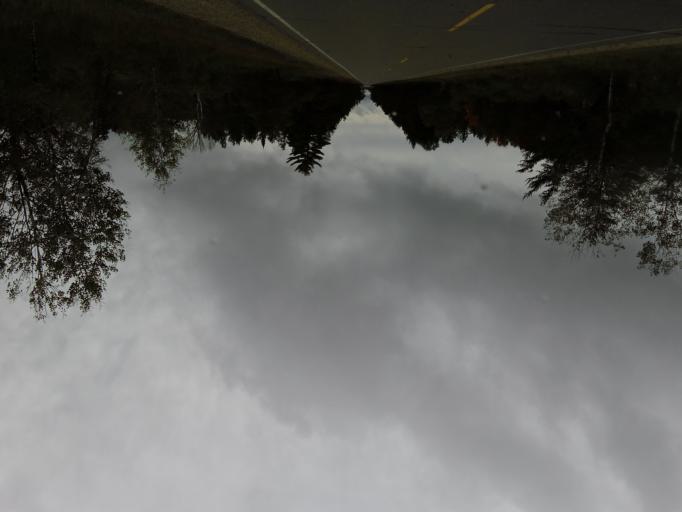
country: US
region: Michigan
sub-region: Roscommon County
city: Roscommon
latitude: 44.4877
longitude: -84.5740
